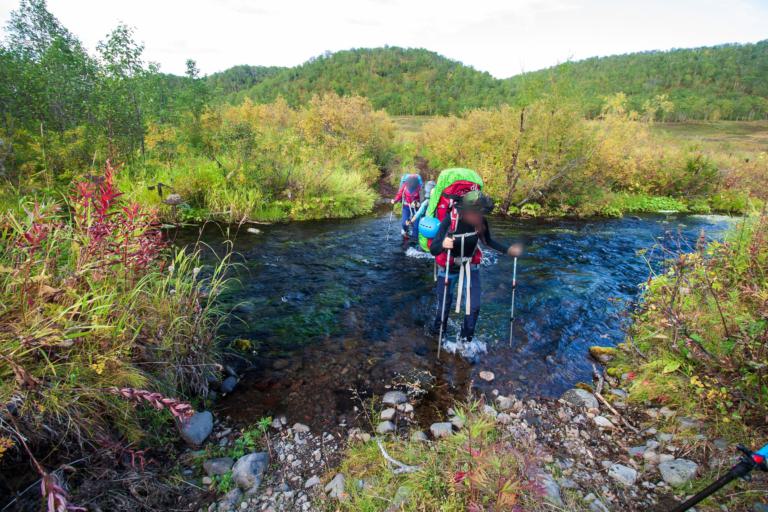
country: RU
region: Kamtsjatka
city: Yelizovo
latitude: 53.7781
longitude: 158.5902
